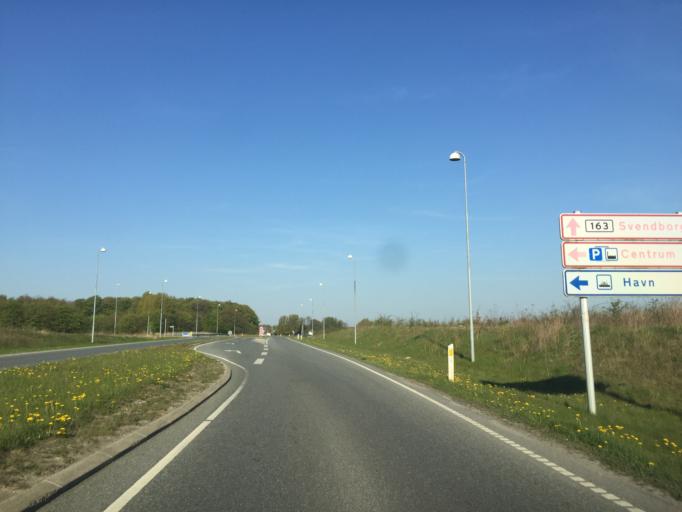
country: DK
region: South Denmark
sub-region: Svendborg Kommune
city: Thuro By
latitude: 55.0782
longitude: 10.6551
